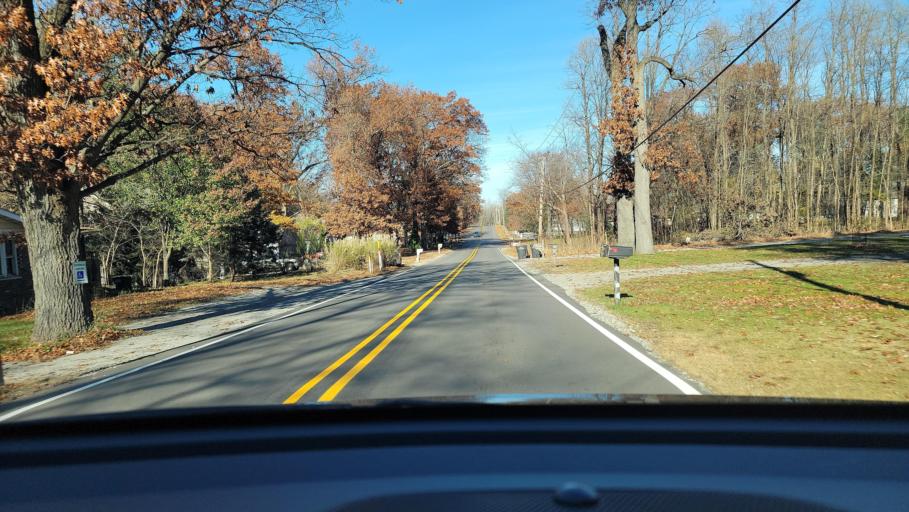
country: US
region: Indiana
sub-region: Porter County
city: Portage
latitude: 41.5864
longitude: -87.1978
